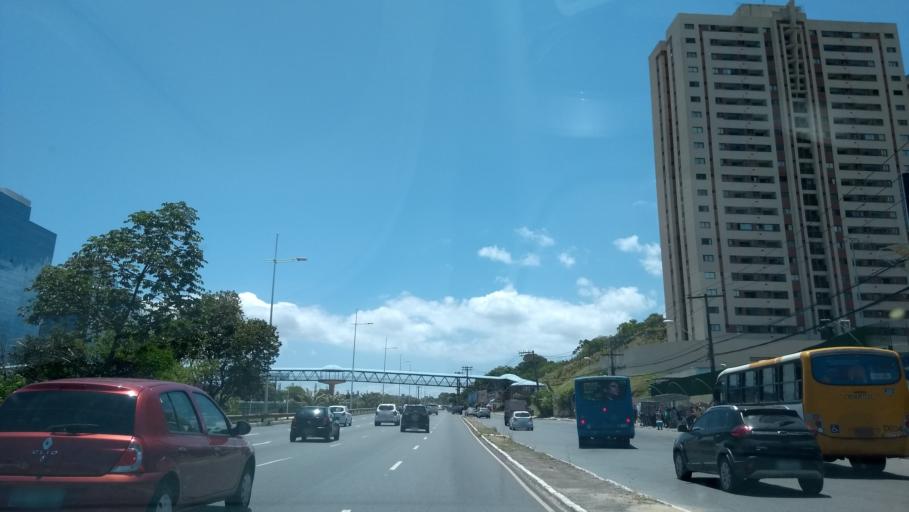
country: BR
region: Bahia
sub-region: Lauro De Freitas
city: Lauro de Freitas
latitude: -12.9383
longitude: -38.4107
